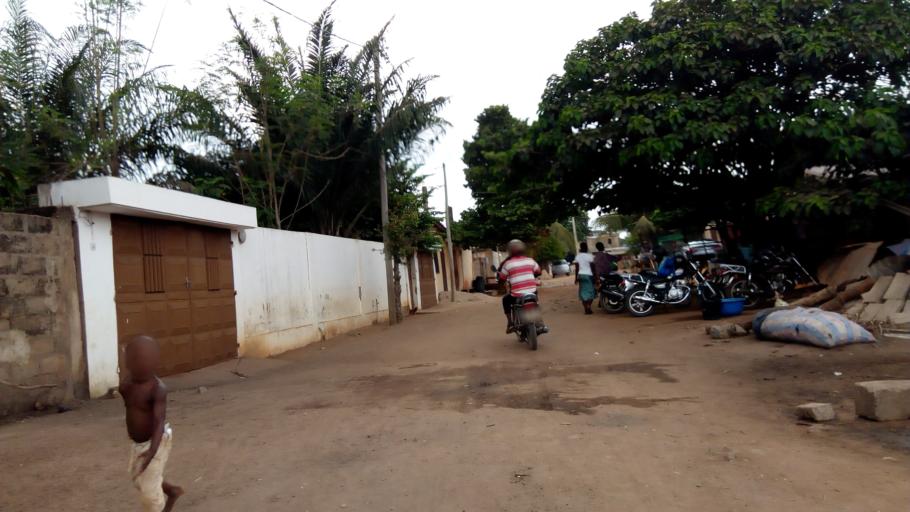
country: TG
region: Maritime
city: Lome
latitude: 6.2172
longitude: 1.1823
